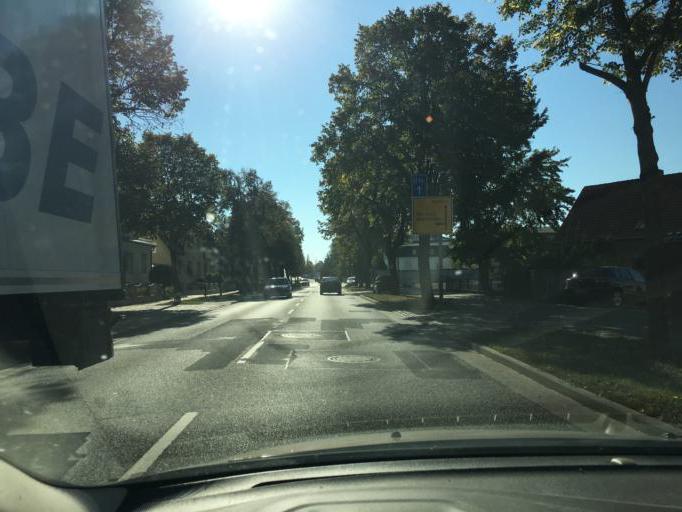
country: DE
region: Saxony-Anhalt
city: Forderstedt
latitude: 51.8947
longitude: 11.6333
